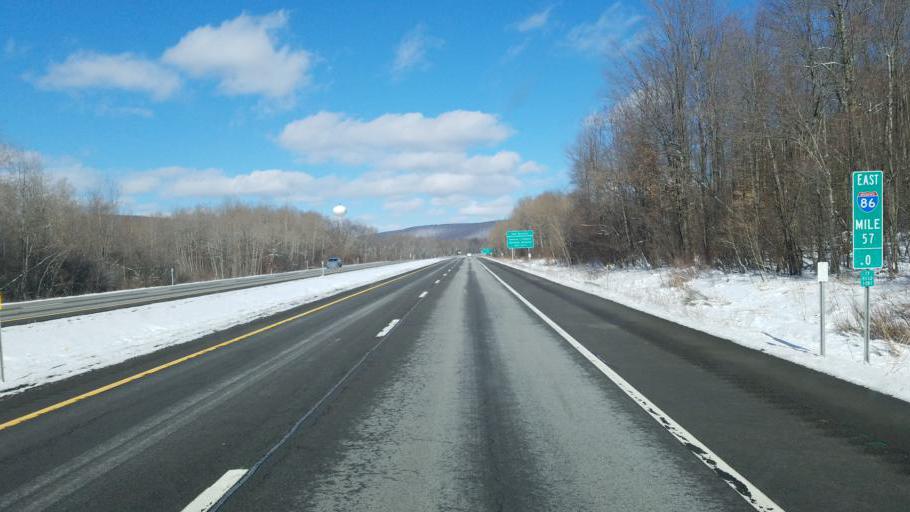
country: US
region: New York
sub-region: Cattaraugus County
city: Salamanca
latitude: 42.1437
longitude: -78.7701
